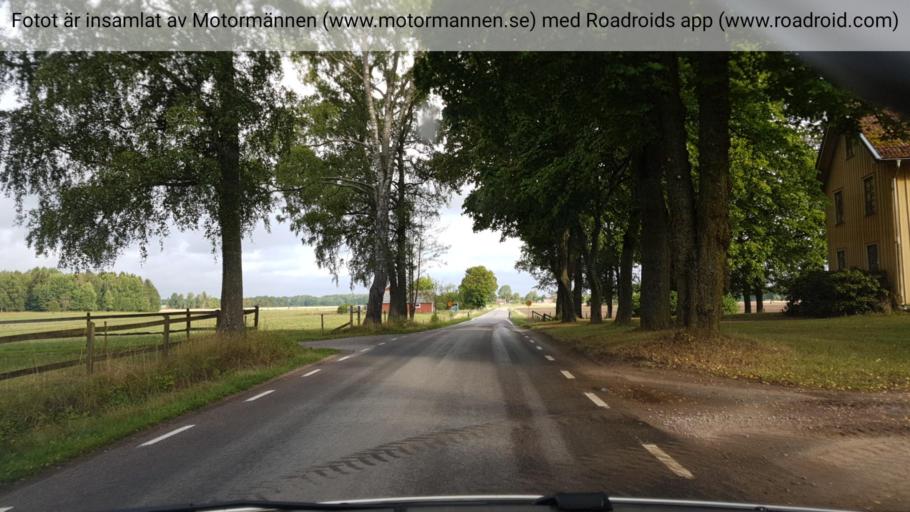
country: SE
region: Vaestra Goetaland
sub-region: Gotene Kommun
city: Kallby
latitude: 58.4636
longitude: 13.3335
